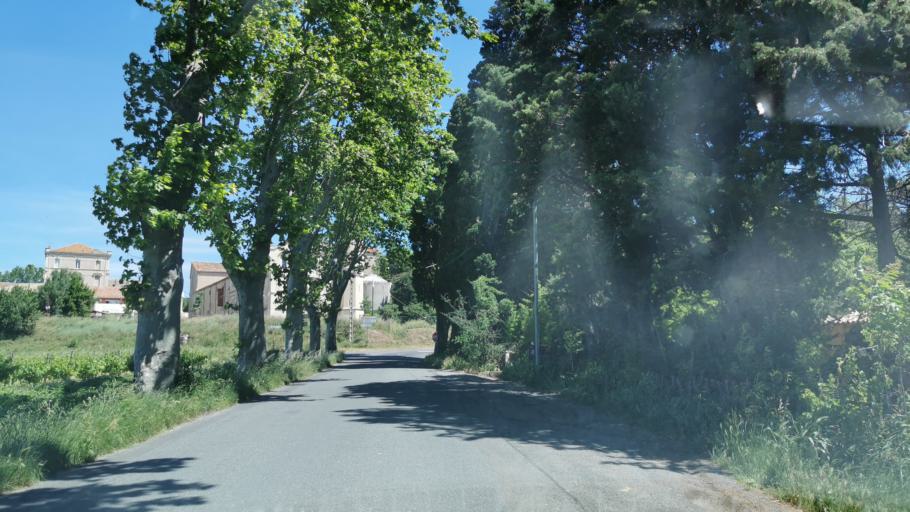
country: FR
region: Languedoc-Roussillon
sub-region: Departement de l'Aude
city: Canet
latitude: 43.2465
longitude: 2.8583
